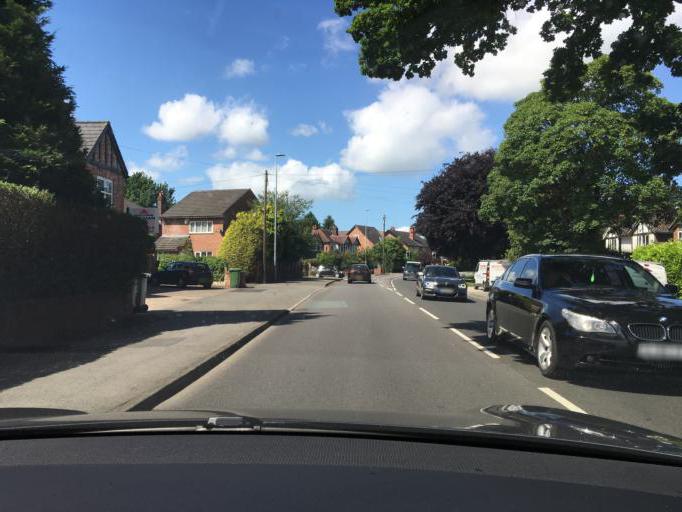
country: GB
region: England
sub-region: Cheshire East
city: Wilmslow
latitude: 53.3270
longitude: -2.2440
